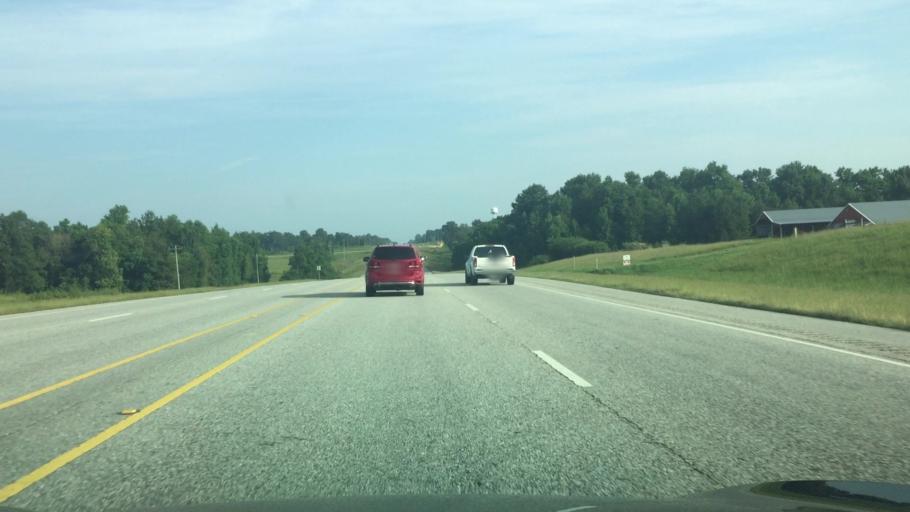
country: US
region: Alabama
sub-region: Butler County
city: Georgiana
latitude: 31.5214
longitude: -86.7141
